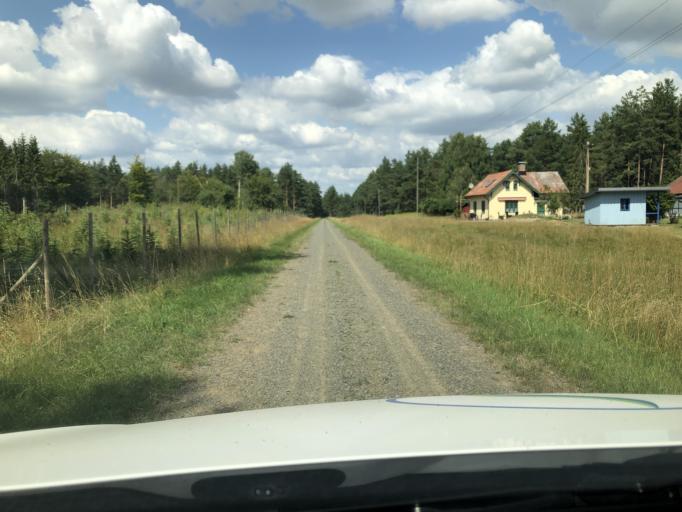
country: SE
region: Skane
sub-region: Kristianstads Kommun
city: Degeberga
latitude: 55.8664
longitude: 14.0809
